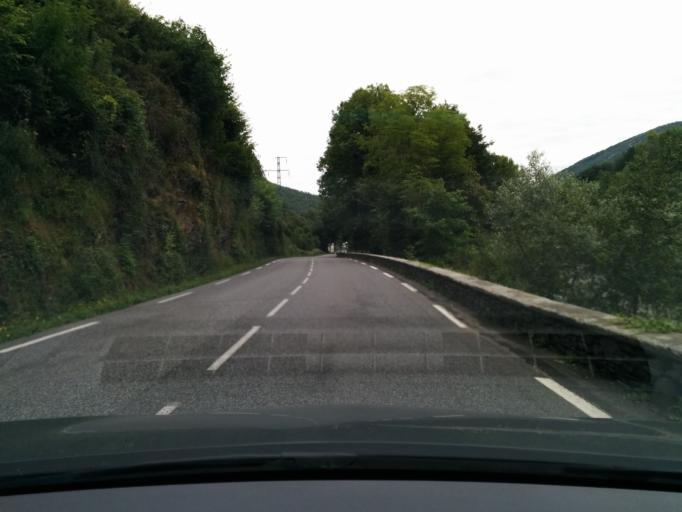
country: FR
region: Midi-Pyrenees
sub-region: Departement des Hautes-Pyrenees
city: La Barthe-de-Neste
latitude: 42.9889
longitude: 0.3750
